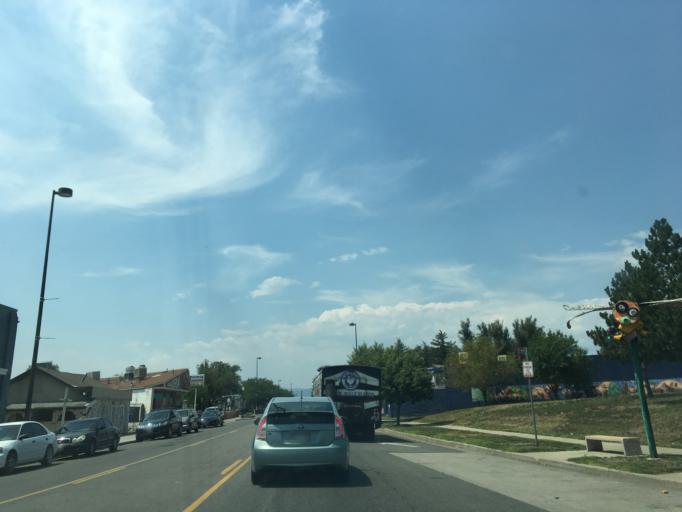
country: US
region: Colorado
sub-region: Jefferson County
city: Lakewood
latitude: 39.7103
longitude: -105.0342
